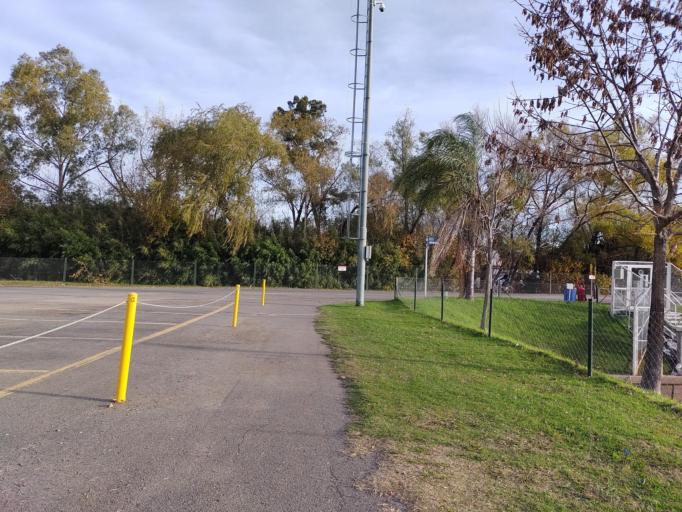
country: AR
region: Buenos Aires
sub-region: Partido de San Isidro
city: San Isidro
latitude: -34.4441
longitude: -58.5318
